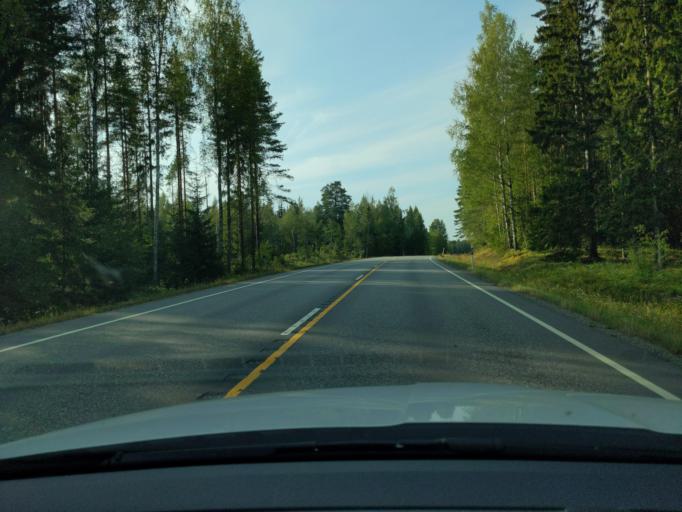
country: FI
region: Paijanne Tavastia
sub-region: Lahti
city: Padasjoki
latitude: 61.3074
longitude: 25.2937
